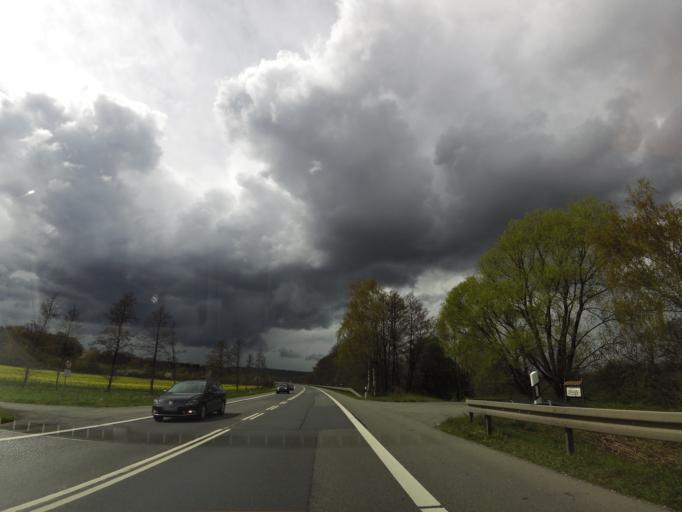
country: DE
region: Lower Saxony
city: Lutter am Barenberge
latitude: 51.9543
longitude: 10.2772
